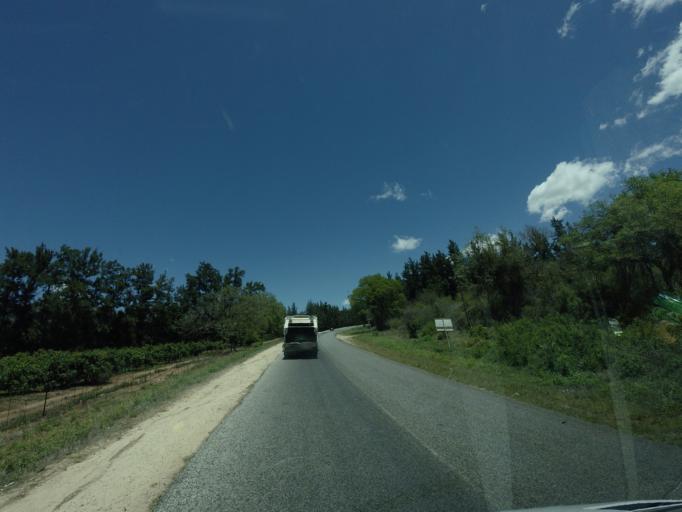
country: ZA
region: Limpopo
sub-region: Mopani District Municipality
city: Hoedspruit
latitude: -24.4077
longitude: 30.7927
